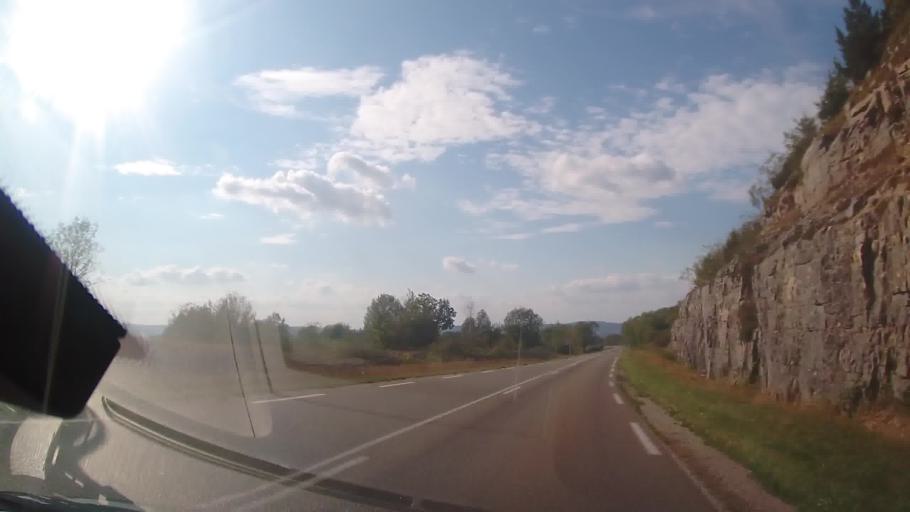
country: FR
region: Franche-Comte
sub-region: Departement du Jura
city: Clairvaux-les-Lacs
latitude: 46.5811
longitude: 5.7740
